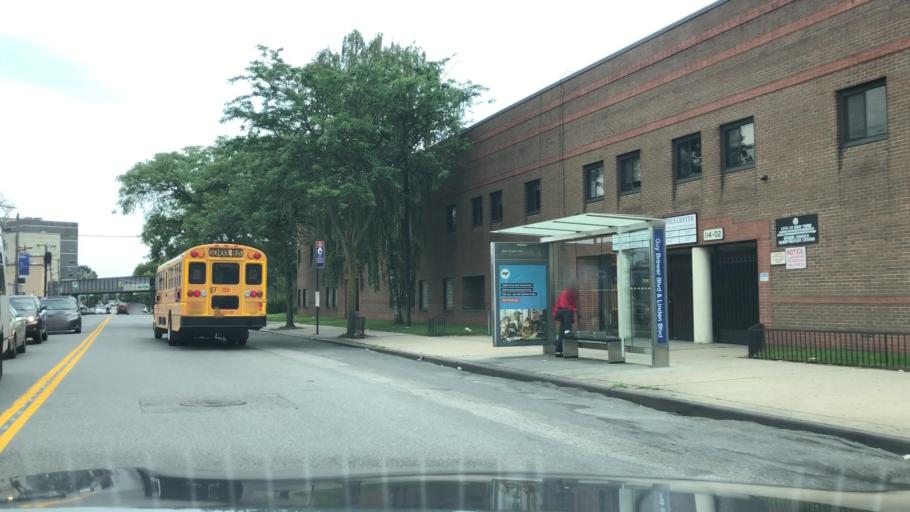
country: US
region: New York
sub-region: Queens County
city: Jamaica
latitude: 40.6889
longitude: -73.7858
